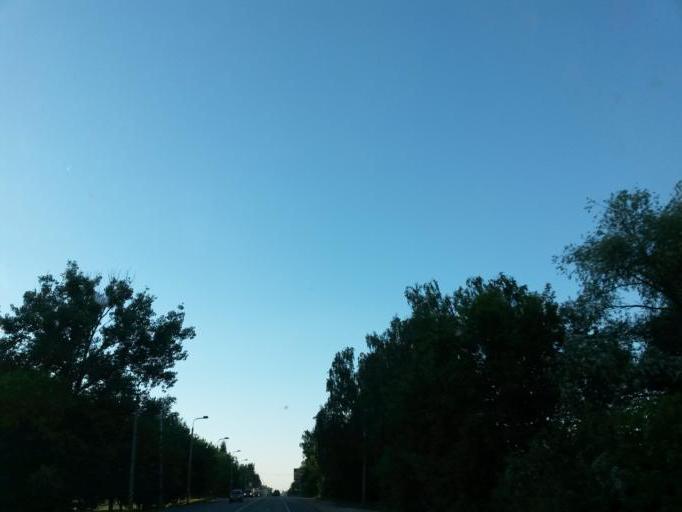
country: RU
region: Moskovskaya
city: Serpukhov
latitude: 54.9365
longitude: 37.4057
